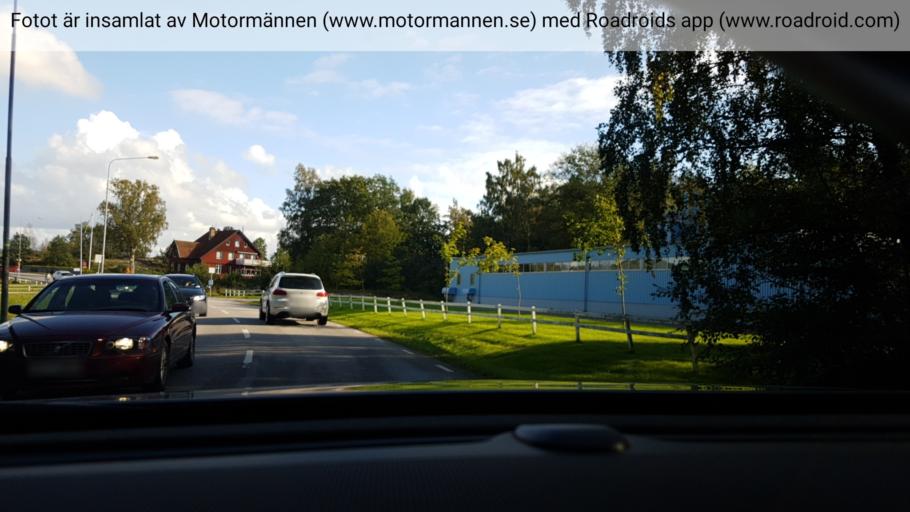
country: SE
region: Vaestra Goetaland
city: Svanesund
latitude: 58.1408
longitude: 11.8287
